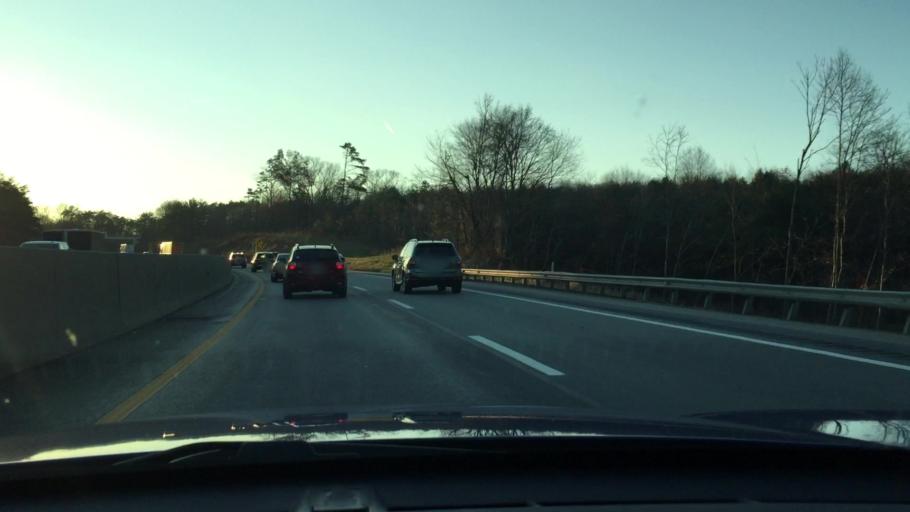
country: US
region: Pennsylvania
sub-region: Fulton County
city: McConnellsburg
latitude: 40.0453
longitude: -78.0243
